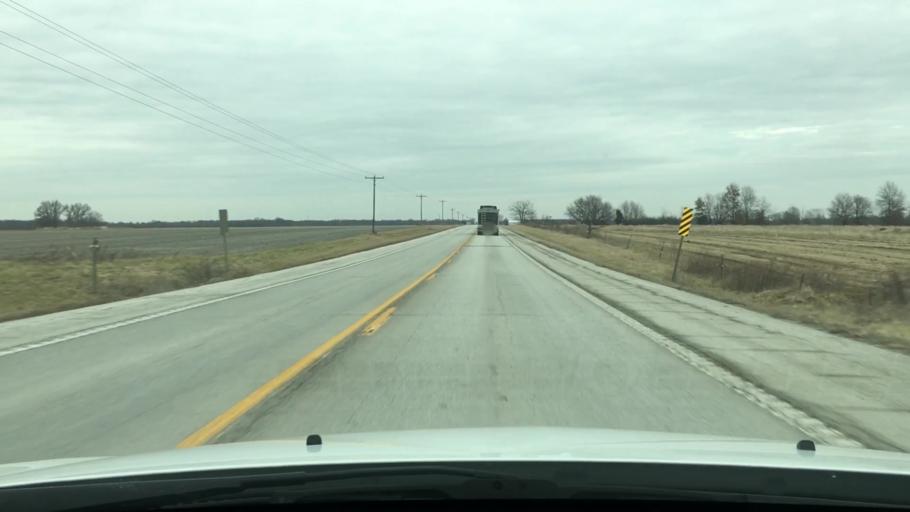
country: US
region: Missouri
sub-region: Montgomery County
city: Wellsville
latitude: 39.1788
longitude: -91.6474
